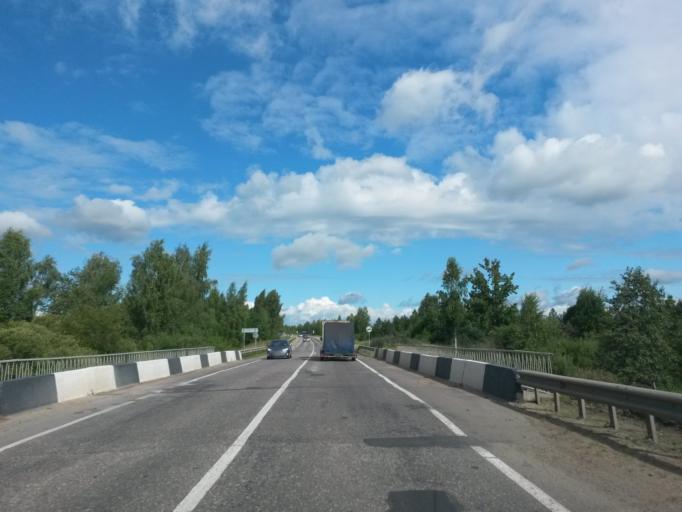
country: RU
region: Jaroslavl
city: Yaroslavl
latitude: 57.5104
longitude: 39.8975
